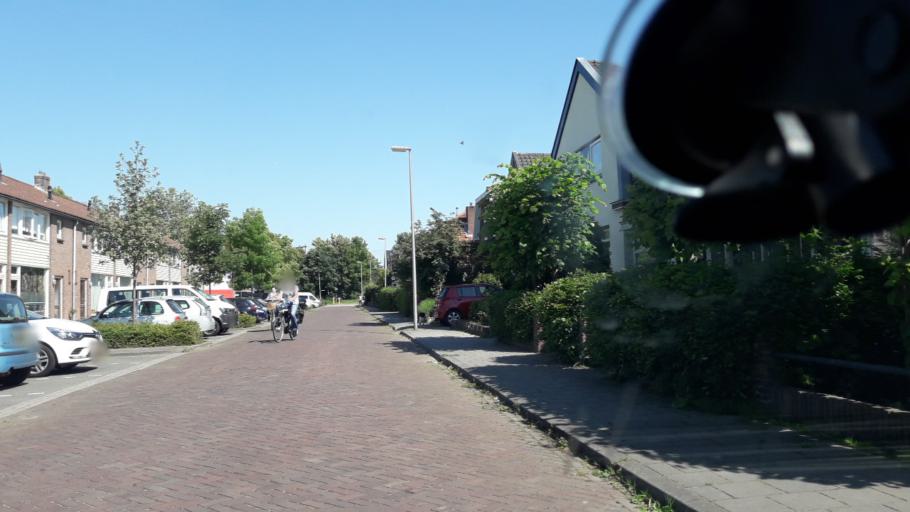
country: NL
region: Overijssel
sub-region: Gemeente Deventer
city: Deventer
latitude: 52.2494
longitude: 6.1399
